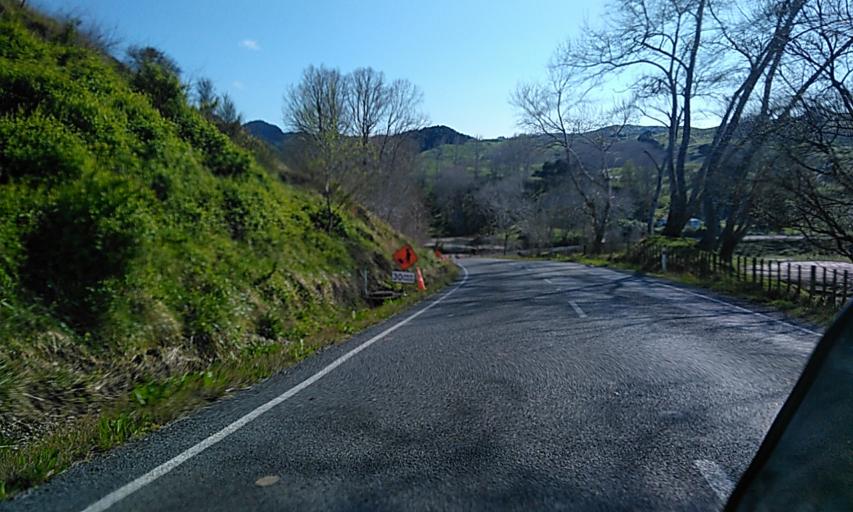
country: NZ
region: Gisborne
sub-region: Gisborne District
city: Gisborne
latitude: -38.5050
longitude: 178.0516
